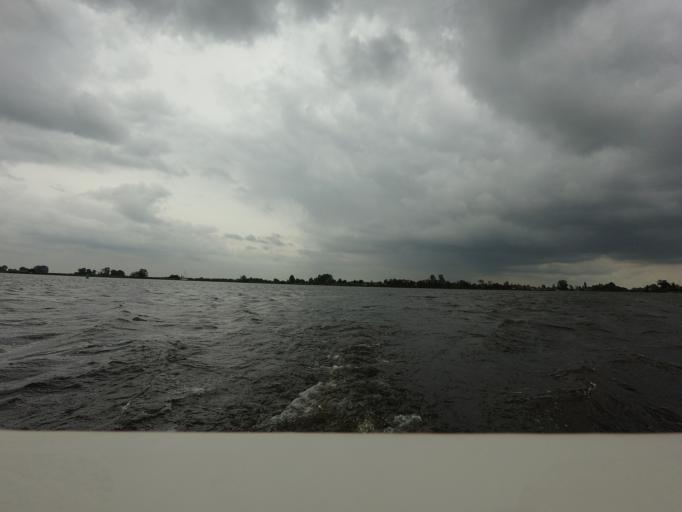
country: NL
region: Friesland
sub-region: Gemeente Smallingerland
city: Oudega
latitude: 53.1037
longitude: 5.9507
